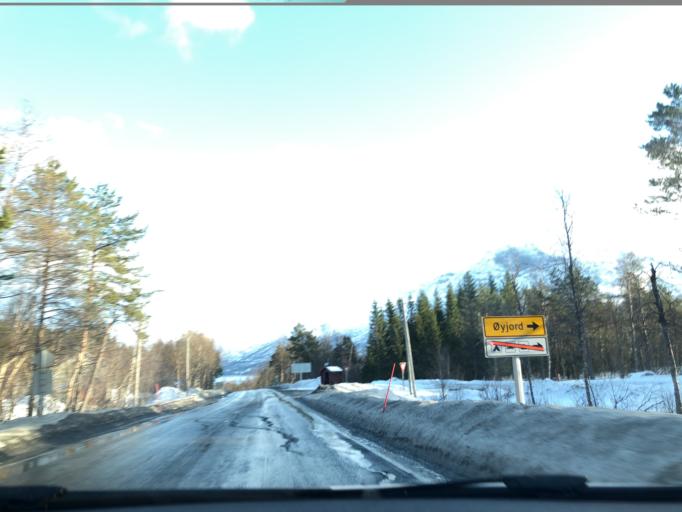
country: NO
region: Nordland
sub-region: Narvik
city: Bjerkvik
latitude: 68.4820
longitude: 17.5348
